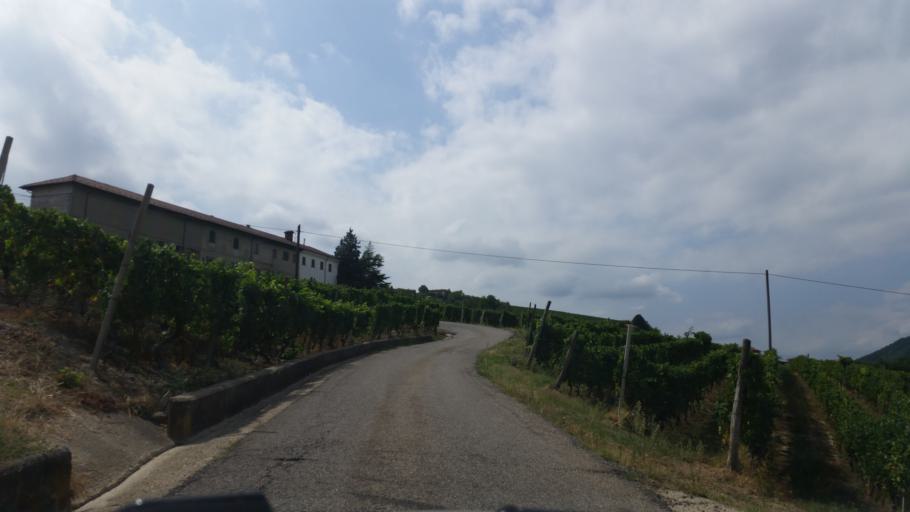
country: IT
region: Piedmont
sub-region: Provincia di Cuneo
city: Cossano Belbo
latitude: 44.6695
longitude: 8.2035
